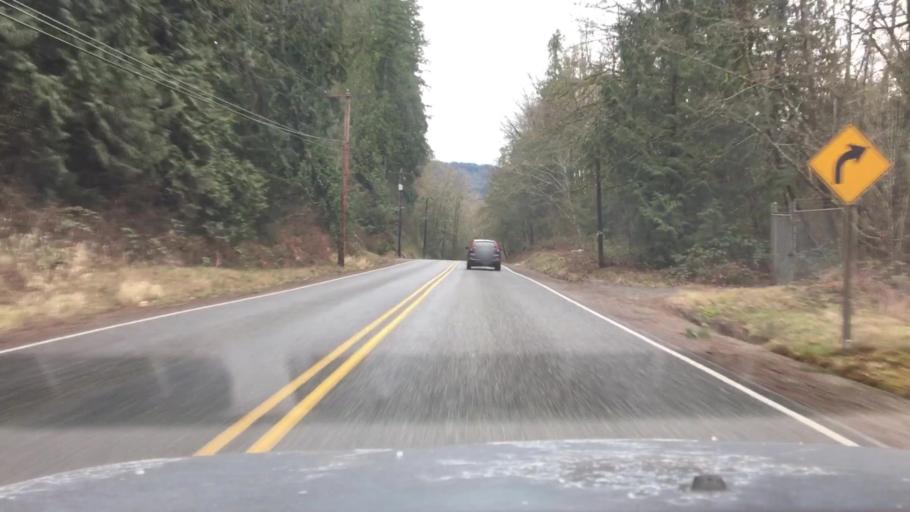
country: US
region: Washington
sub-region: Whatcom County
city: Sudden Valley
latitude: 48.6211
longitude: -122.3294
